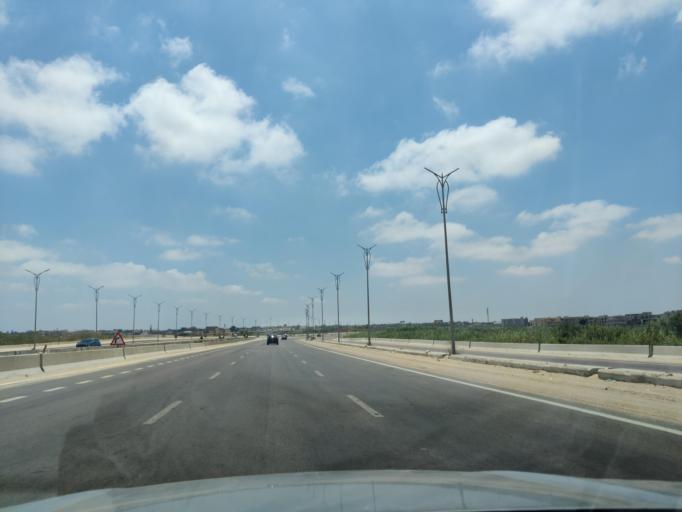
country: EG
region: Alexandria
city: Alexandria
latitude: 30.9873
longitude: 29.6551
